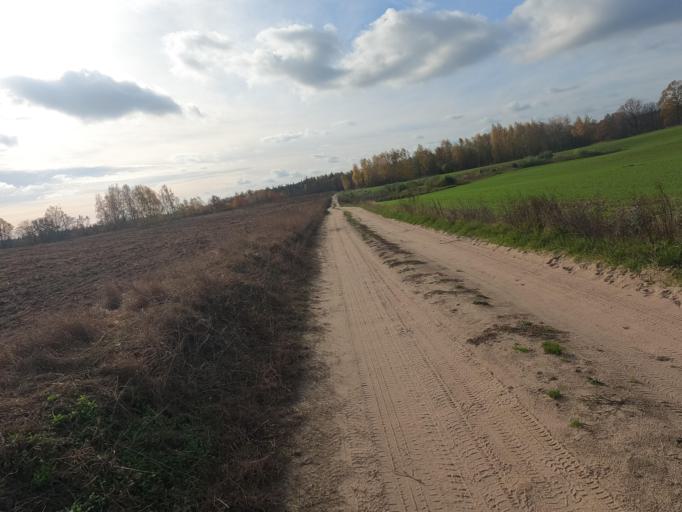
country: PL
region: Pomeranian Voivodeship
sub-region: Powiat starogardzki
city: Starogard Gdanski
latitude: 53.9752
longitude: 18.4836
